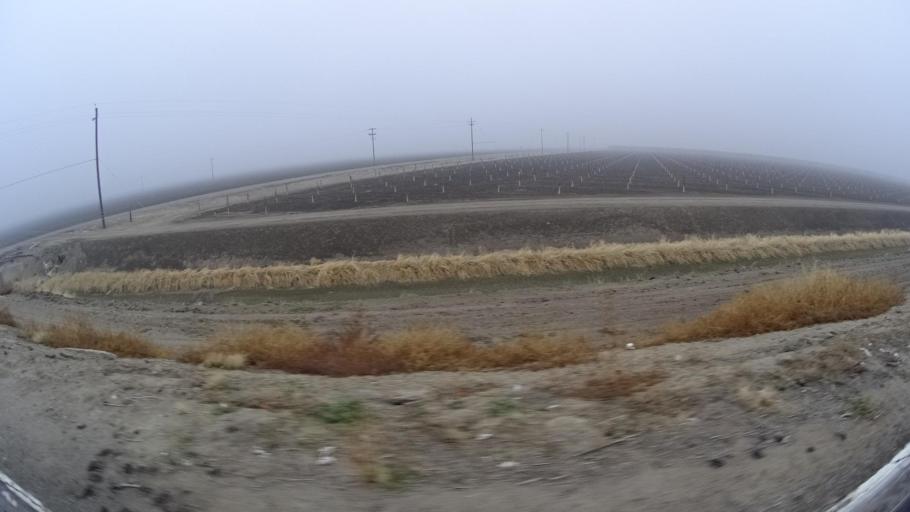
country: US
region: California
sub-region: Kern County
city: Buttonwillow
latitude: 35.4410
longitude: -119.5497
